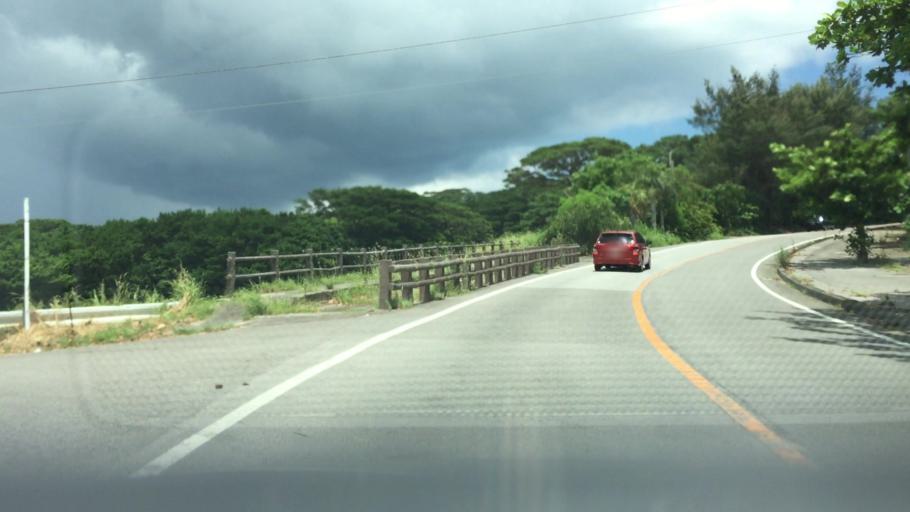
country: JP
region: Okinawa
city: Ishigaki
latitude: 24.4351
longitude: 124.1199
